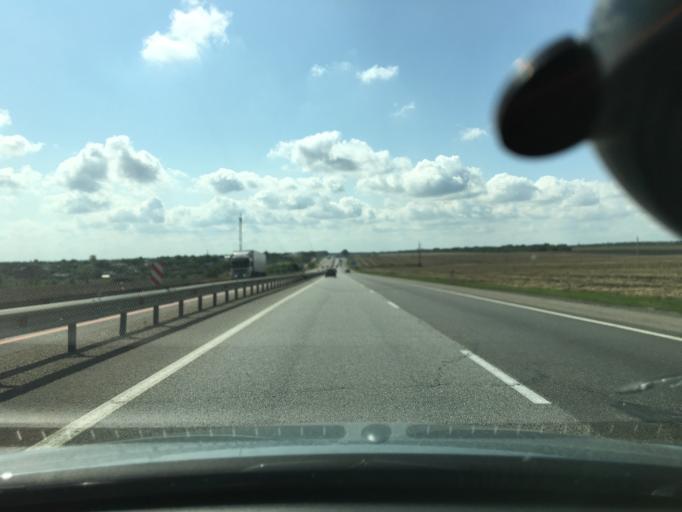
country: RU
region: Krasnodarskiy
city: Krasnoye
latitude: 46.7202
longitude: 39.6542
